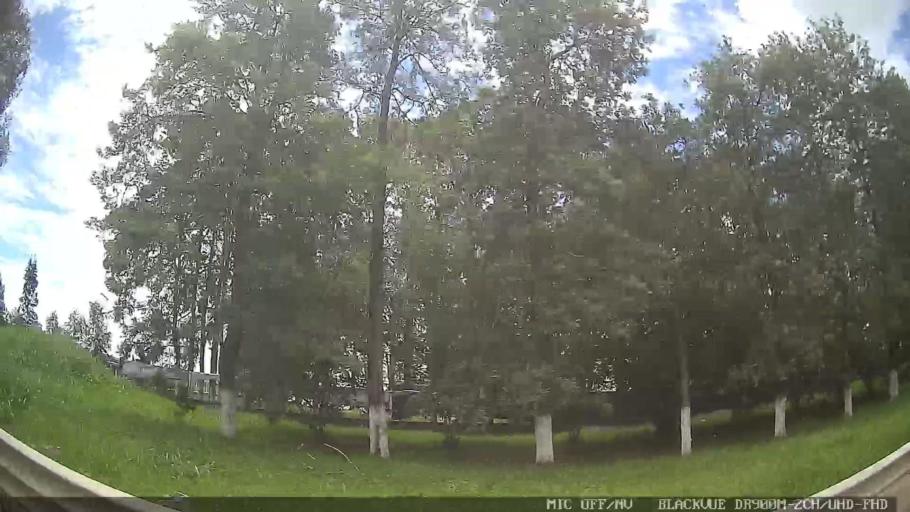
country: BR
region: Sao Paulo
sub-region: Conchas
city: Conchas
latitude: -23.0451
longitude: -47.9360
